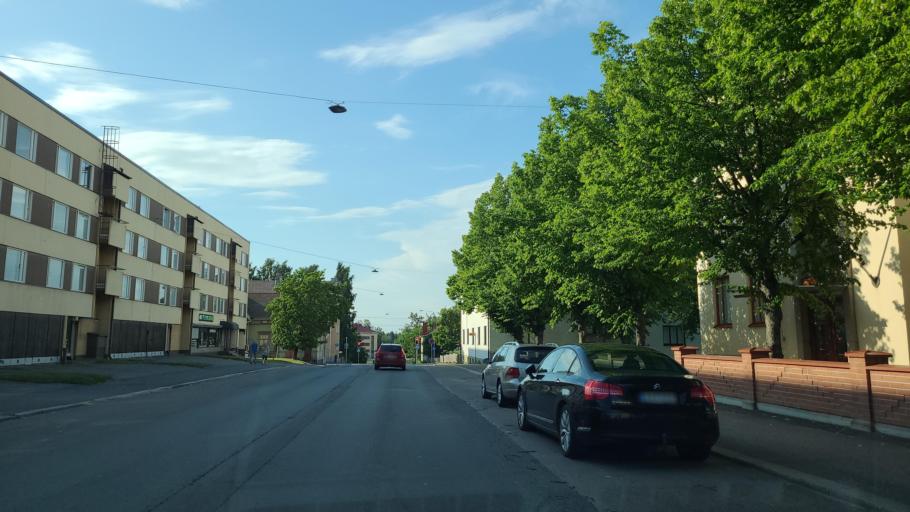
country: FI
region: Ostrobothnia
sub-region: Vaasa
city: Vaasa
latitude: 63.1028
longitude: 21.6195
